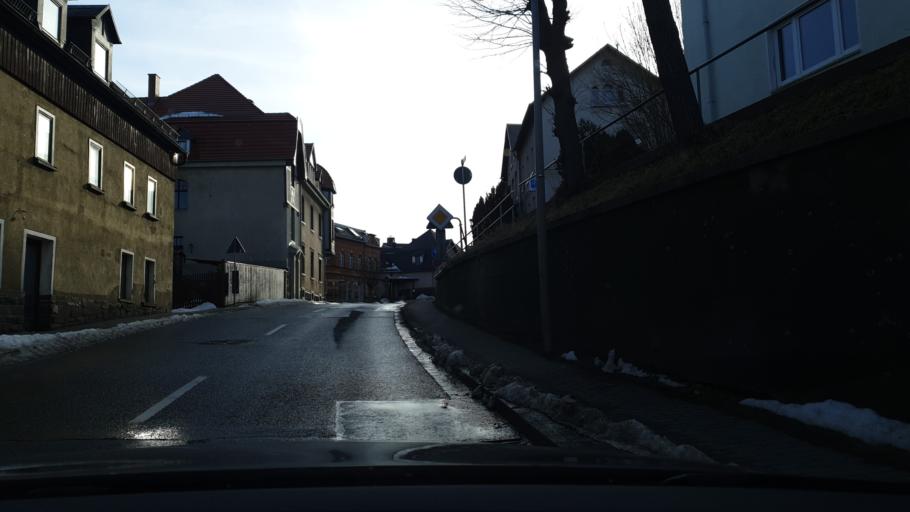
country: DE
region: Thuringia
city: Triebes
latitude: 50.6856
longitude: 12.0230
